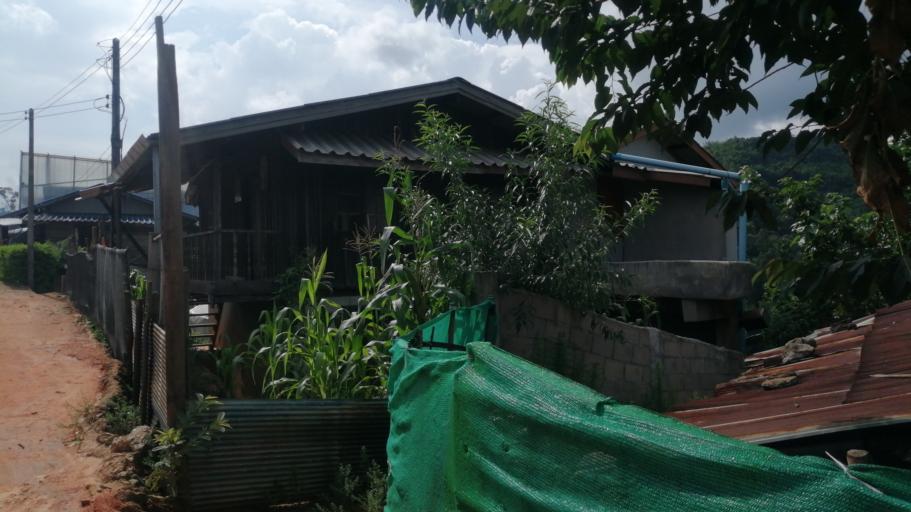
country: TH
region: Chiang Mai
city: Phrao
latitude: 19.5095
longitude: 99.3378
